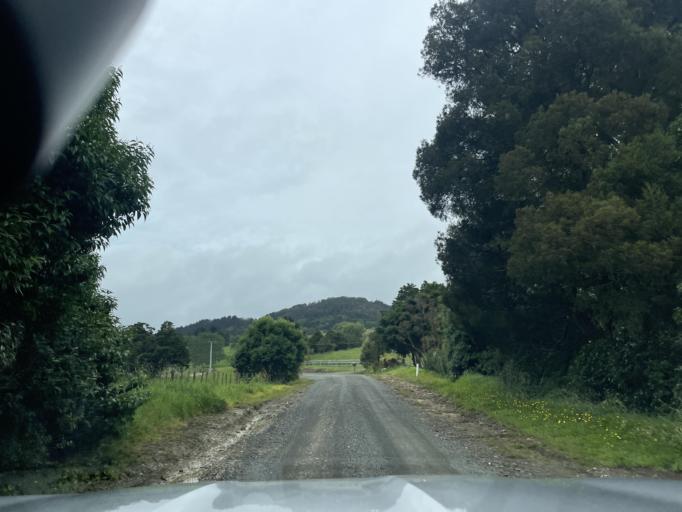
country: NZ
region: Northland
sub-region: Whangarei
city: Ruakaka
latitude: -36.0984
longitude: 174.4147
